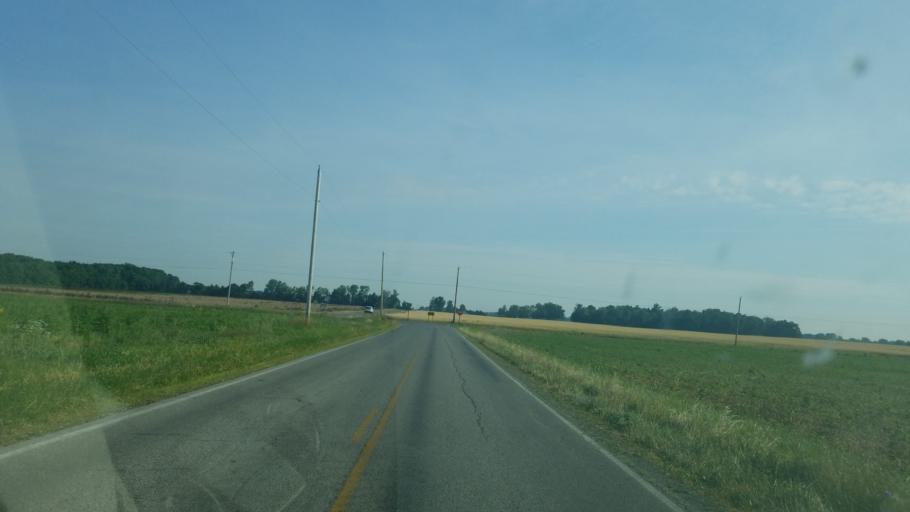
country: US
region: Ohio
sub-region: Hancock County
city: Arlington
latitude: 40.9059
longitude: -83.6985
